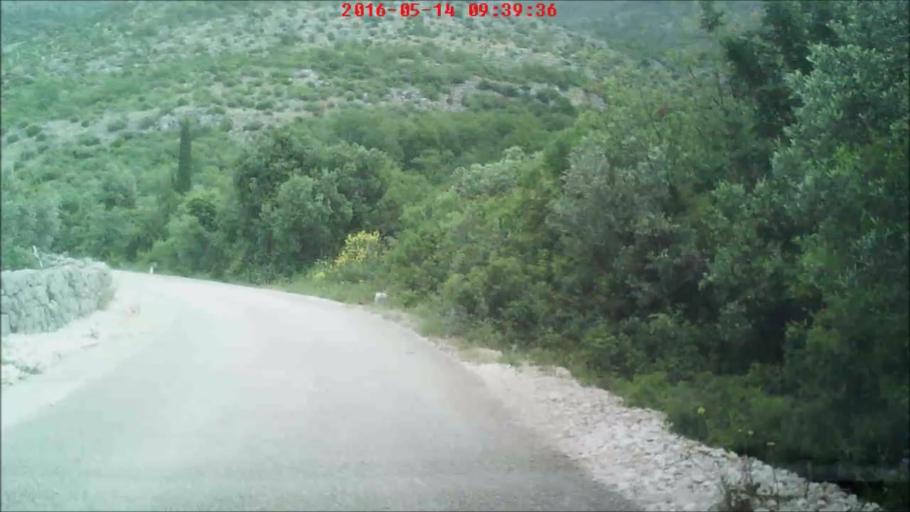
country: HR
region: Dubrovacko-Neretvanska
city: Podgora
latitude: 42.7906
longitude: 17.8921
